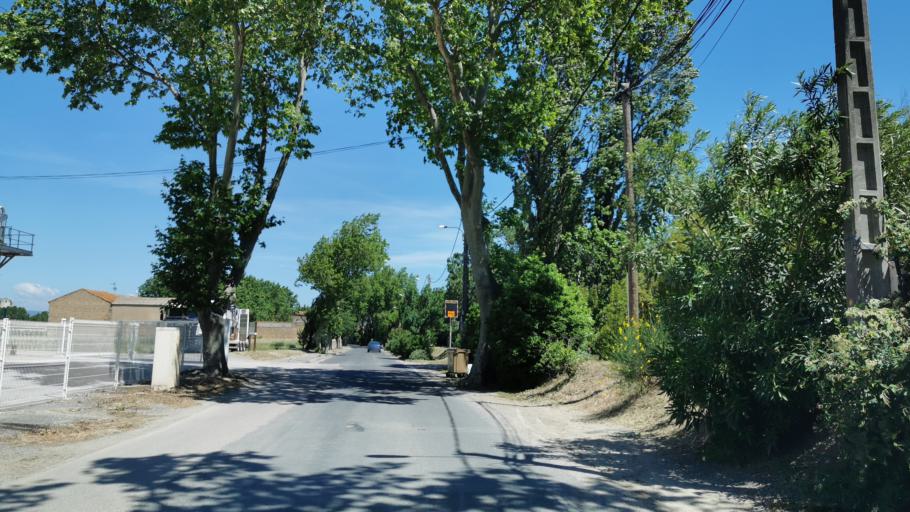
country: FR
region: Languedoc-Roussillon
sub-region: Departement de l'Aude
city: Canet
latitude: 43.2231
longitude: 2.8464
